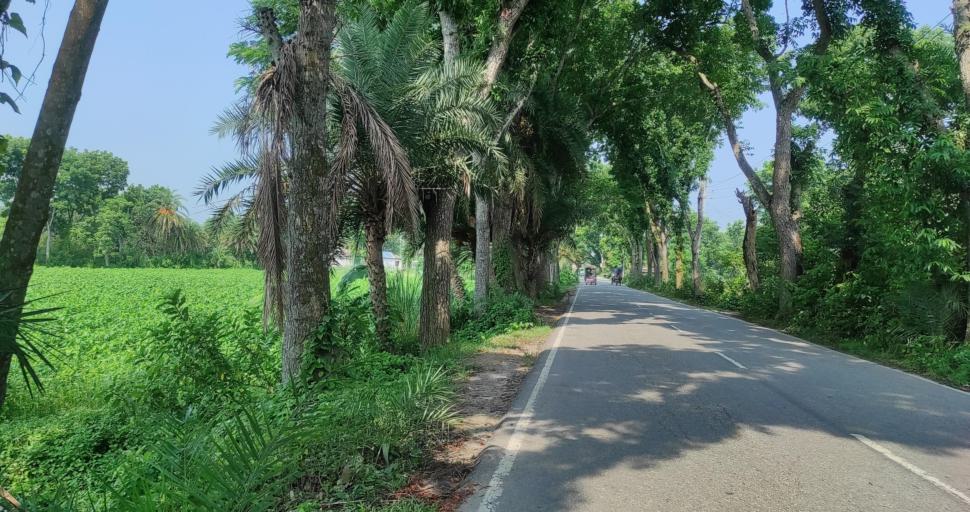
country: BD
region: Rajshahi
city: Ishurdi
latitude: 24.2880
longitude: 89.0679
